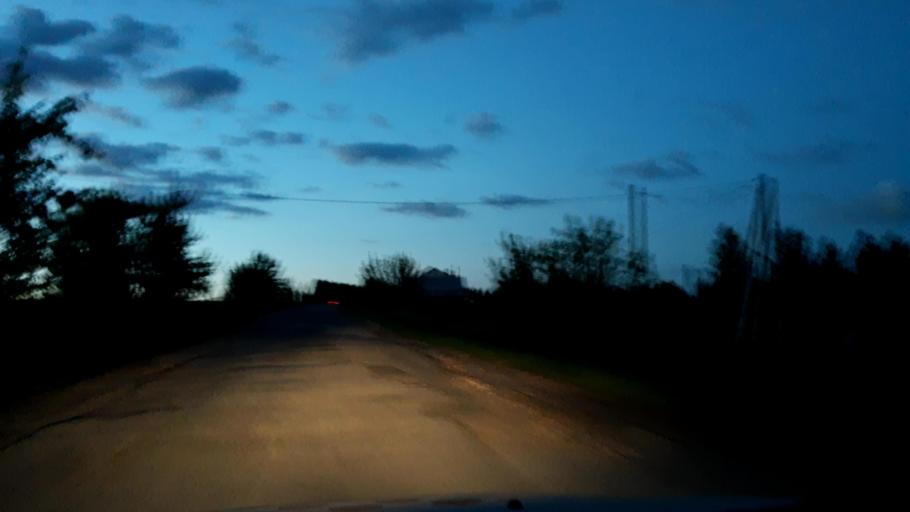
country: RU
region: Nizjnij Novgorod
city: Pamyat' Parizhskoy Kommuny
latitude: 56.0474
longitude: 44.4358
